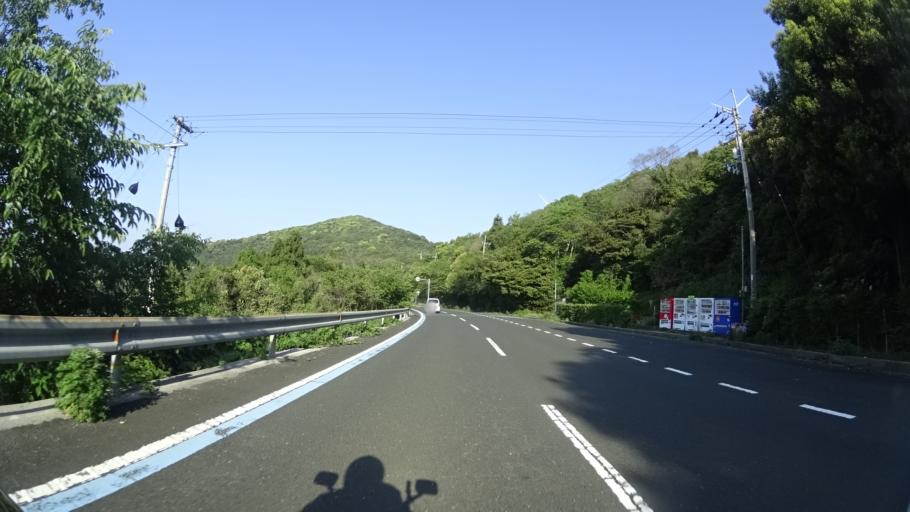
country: JP
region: Ehime
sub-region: Nishiuwa-gun
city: Ikata-cho
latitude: 33.4197
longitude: 132.1875
